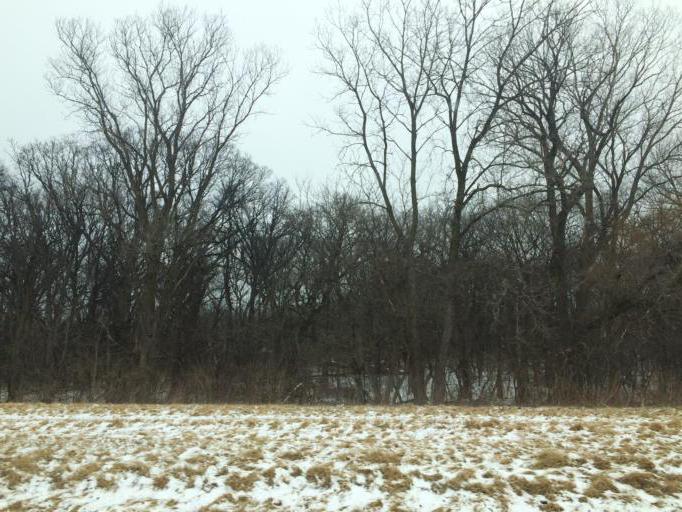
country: US
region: Illinois
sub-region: McHenry County
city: Woodstock
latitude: 42.3068
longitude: -88.4714
